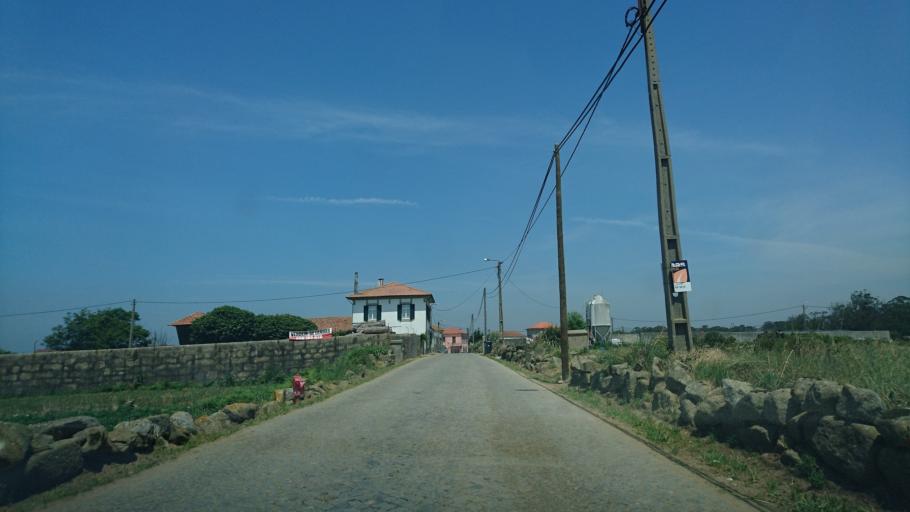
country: PT
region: Porto
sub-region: Matosinhos
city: Lavra
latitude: 41.2648
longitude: -8.7084
